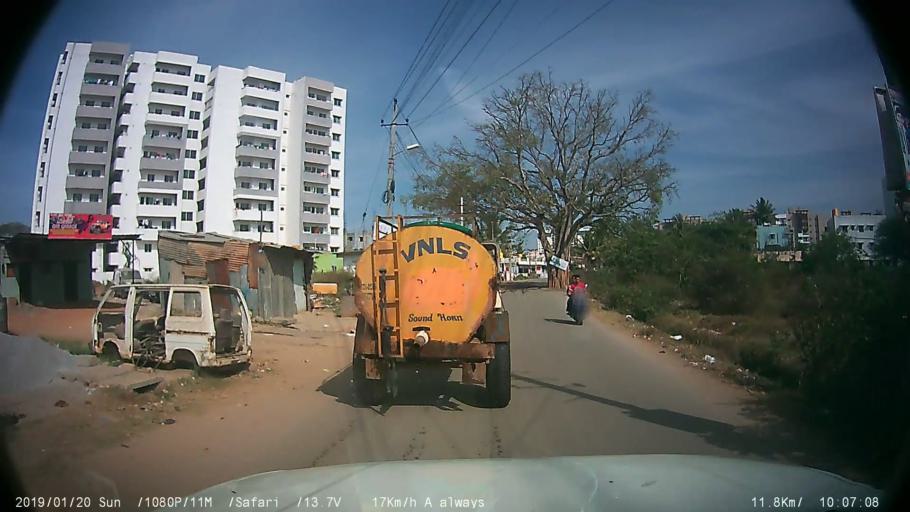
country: IN
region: Karnataka
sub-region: Bangalore Urban
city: Anekal
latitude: 12.8295
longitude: 77.6552
